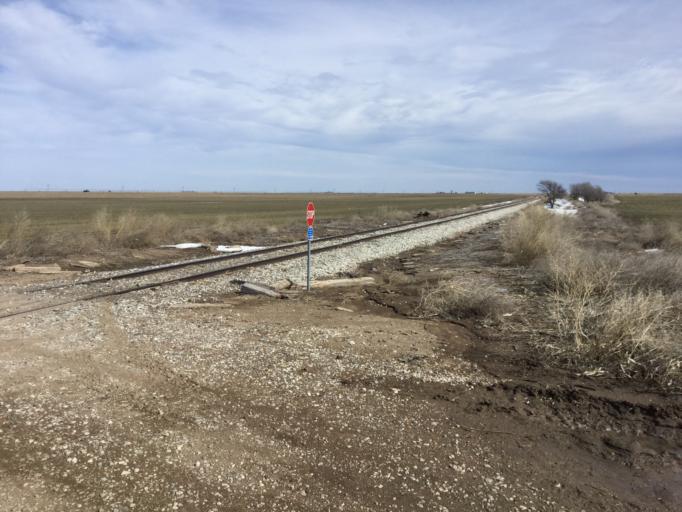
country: US
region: Kansas
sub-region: Lane County
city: Dighton
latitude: 38.4868
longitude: -100.4492
